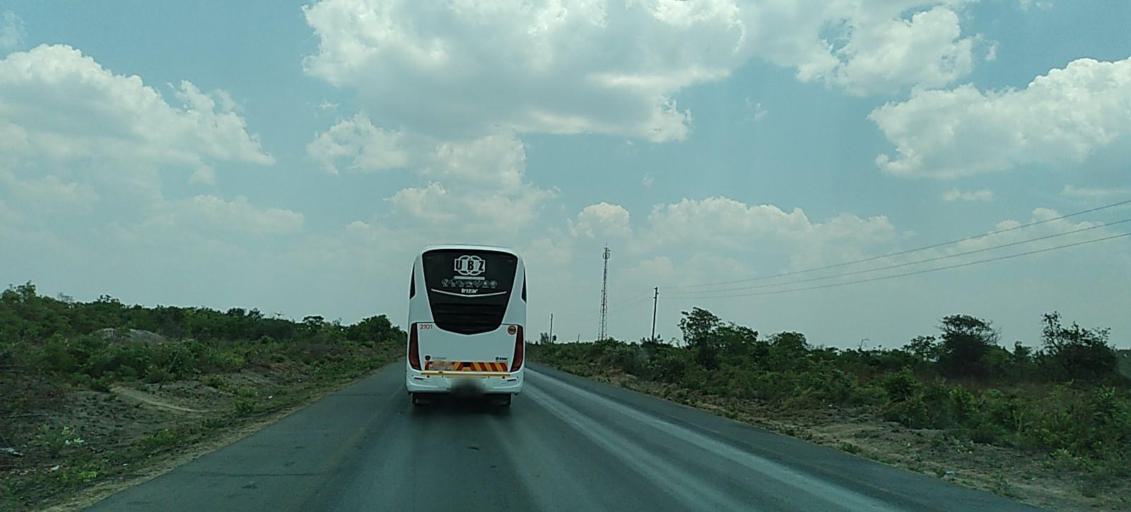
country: ZM
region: Central
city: Kapiri Mposhi
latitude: -14.0636
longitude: 28.6435
